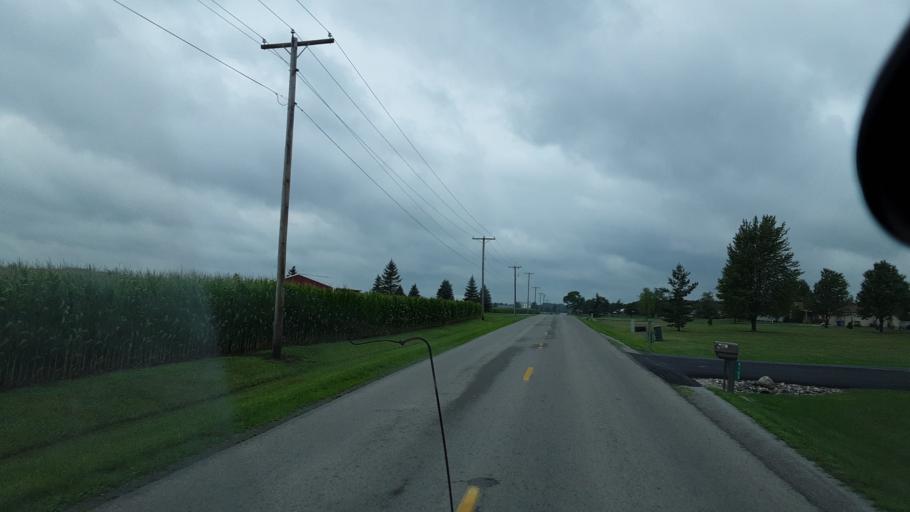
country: US
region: Indiana
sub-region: Allen County
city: New Haven
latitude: 40.9472
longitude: -85.0322
